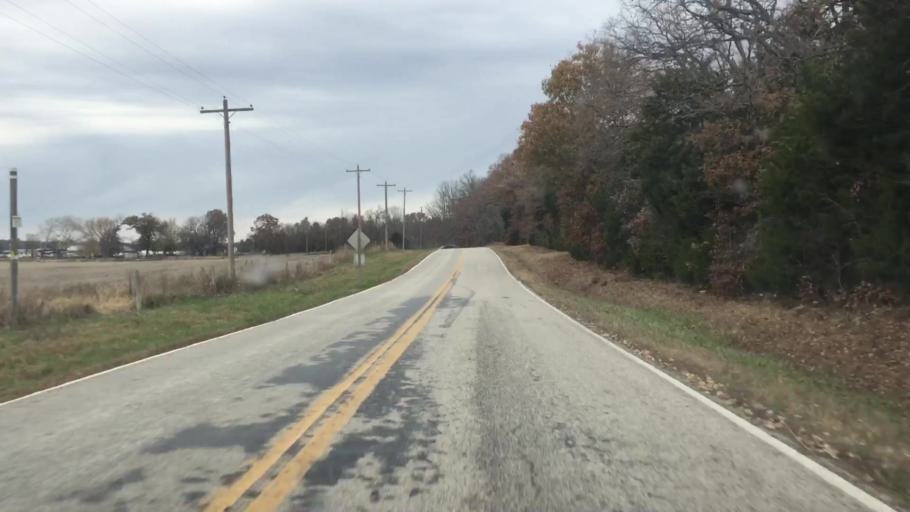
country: US
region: Missouri
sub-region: Saint Clair County
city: Osceola
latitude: 37.9884
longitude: -93.6450
